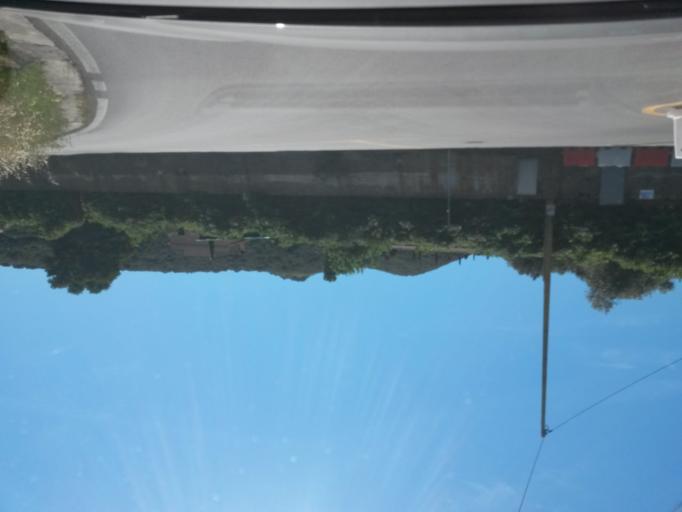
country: IT
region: Tuscany
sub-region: Provincia di Livorno
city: Portoferraio
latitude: 42.7957
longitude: 10.3178
